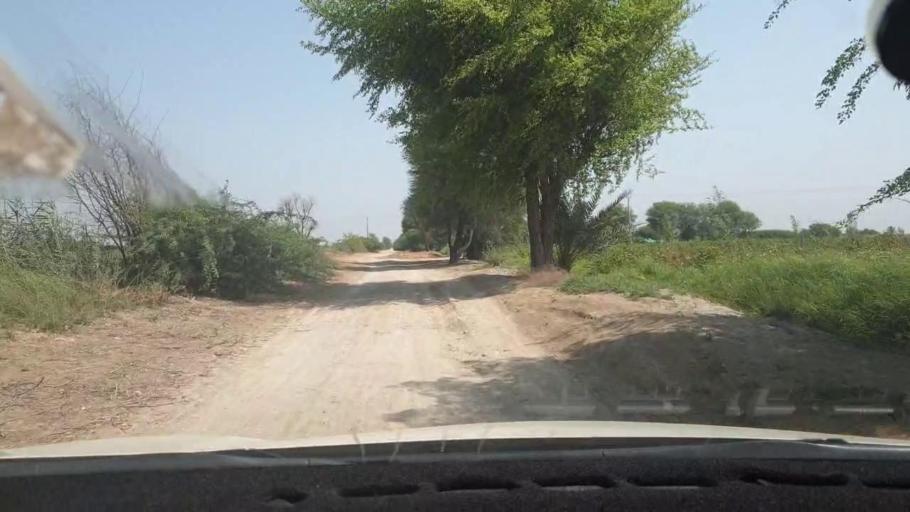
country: PK
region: Sindh
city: Tando Mittha Khan
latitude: 25.9167
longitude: 69.2369
